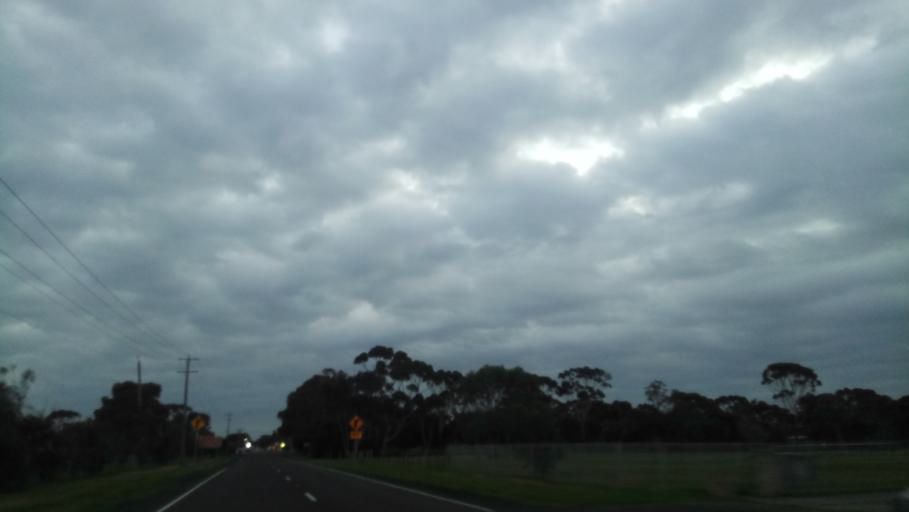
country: AU
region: Victoria
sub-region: Wyndham
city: Point Cook
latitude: -37.9200
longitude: 144.7501
